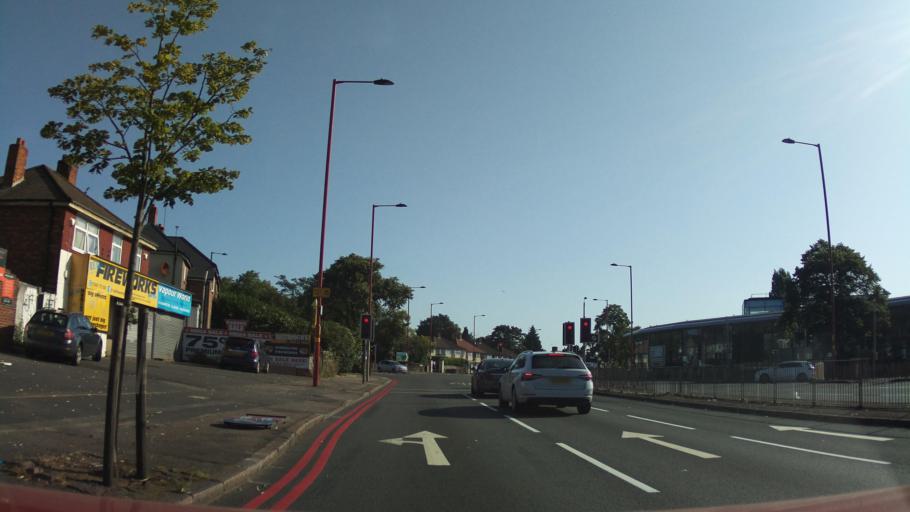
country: GB
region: England
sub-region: City and Borough of Birmingham
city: Sutton Coldfield
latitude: 52.5105
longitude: -1.8345
